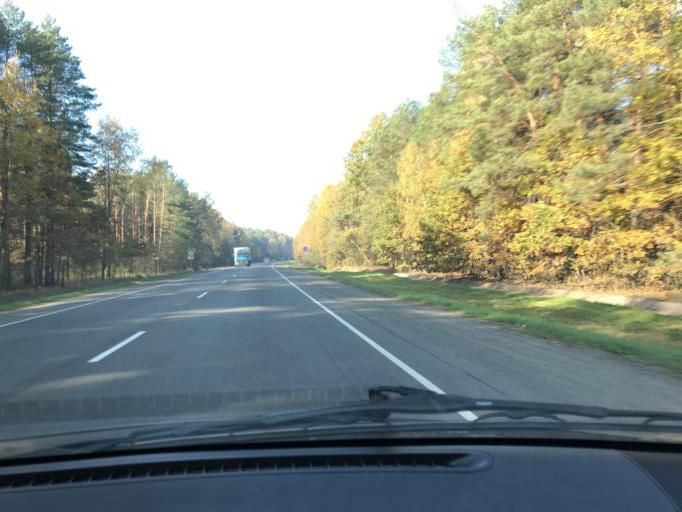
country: BY
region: Brest
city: Luninyets
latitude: 52.2777
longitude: 26.8460
